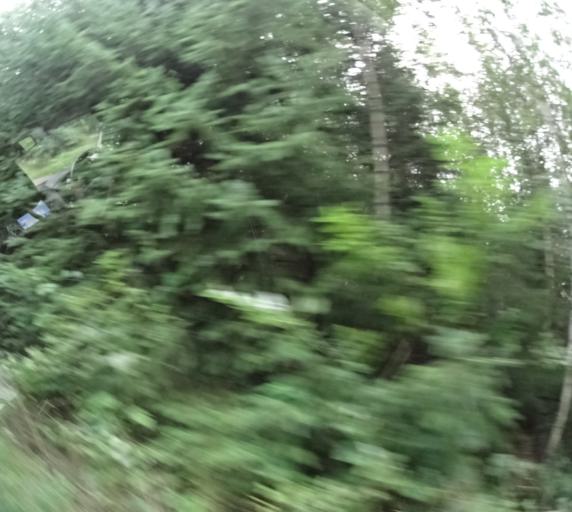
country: DK
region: Central Jutland
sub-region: Syddjurs Kommune
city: Ryomgard
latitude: 56.4173
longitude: 10.5597
